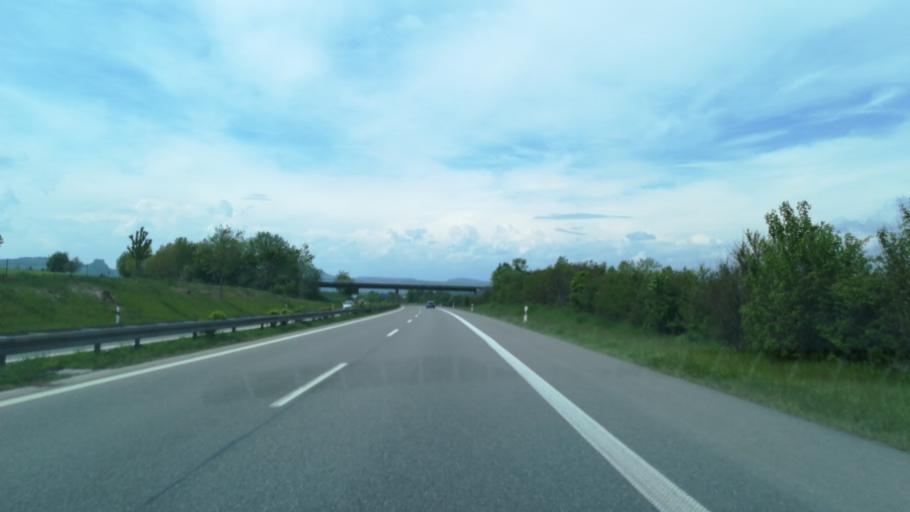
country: DE
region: Baden-Wuerttemberg
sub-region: Freiburg Region
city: Volkertshausen
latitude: 47.7900
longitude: 8.8860
